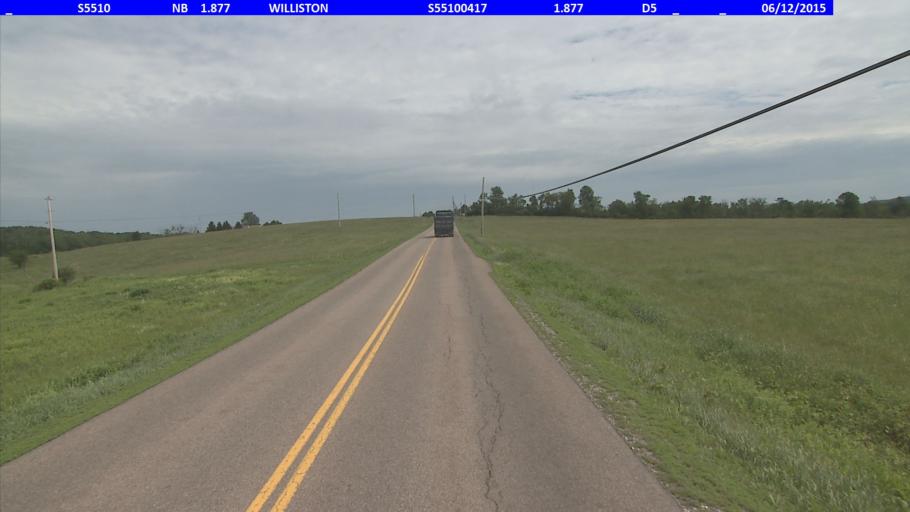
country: US
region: Vermont
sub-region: Chittenden County
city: Williston
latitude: 44.3990
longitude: -73.0921
